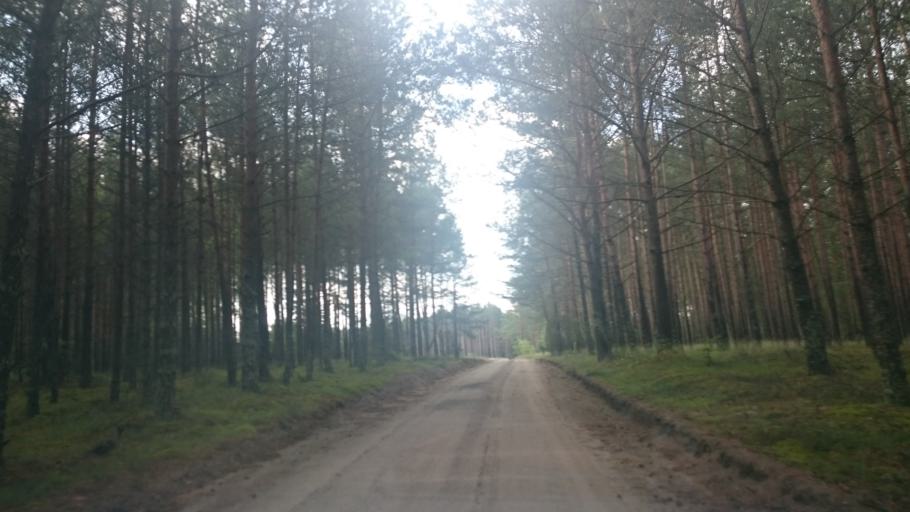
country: PL
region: Pomeranian Voivodeship
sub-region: Powiat koscierski
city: Karsin
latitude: 53.9928
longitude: 17.9339
